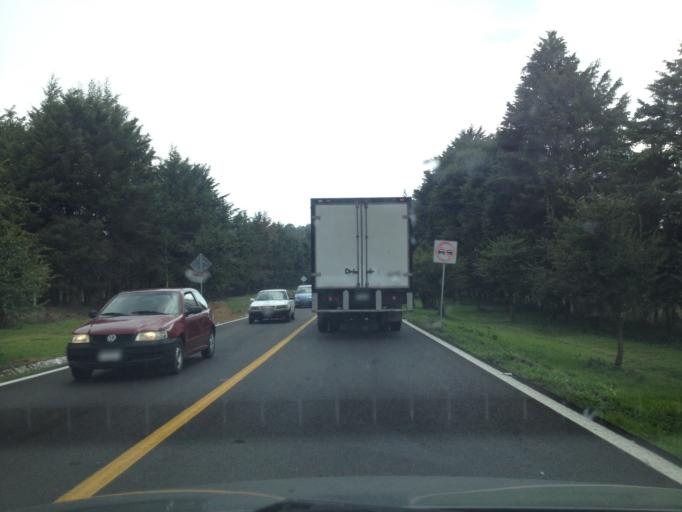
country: MX
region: Michoacan
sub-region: Patzcuaro
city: Santa Maria Huiramangaro (San Juan Tumbio)
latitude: 19.4923
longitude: -101.7452
